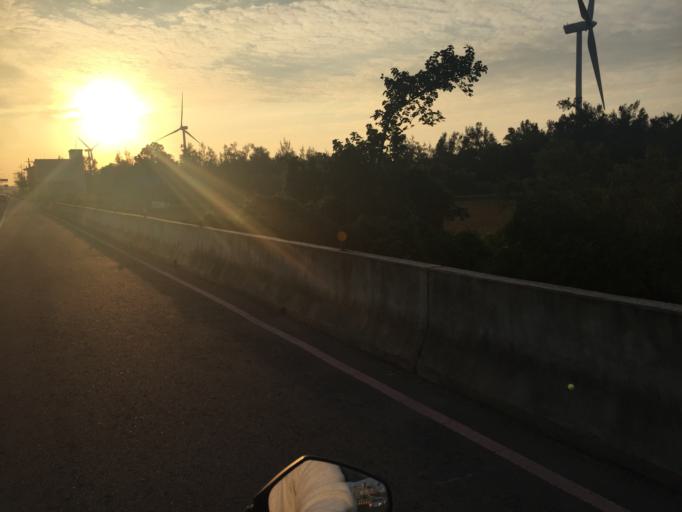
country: TW
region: Taiwan
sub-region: Hsinchu
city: Hsinchu
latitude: 24.7392
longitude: 120.8900
